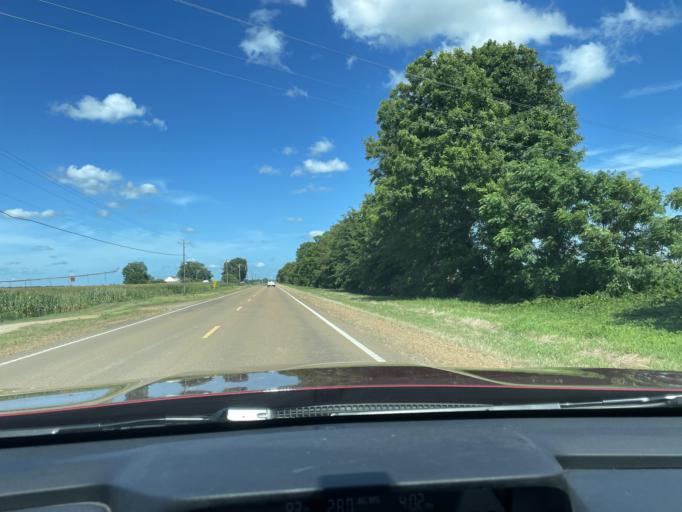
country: US
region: Mississippi
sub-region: Humphreys County
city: Belzoni
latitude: 33.1838
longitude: -90.5277
